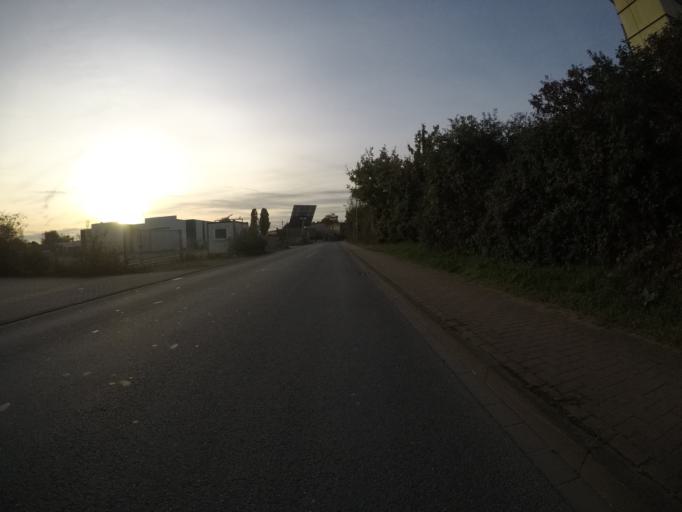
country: DE
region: North Rhine-Westphalia
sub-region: Regierungsbezirk Munster
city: Rhede
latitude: 51.8279
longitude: 6.7101
